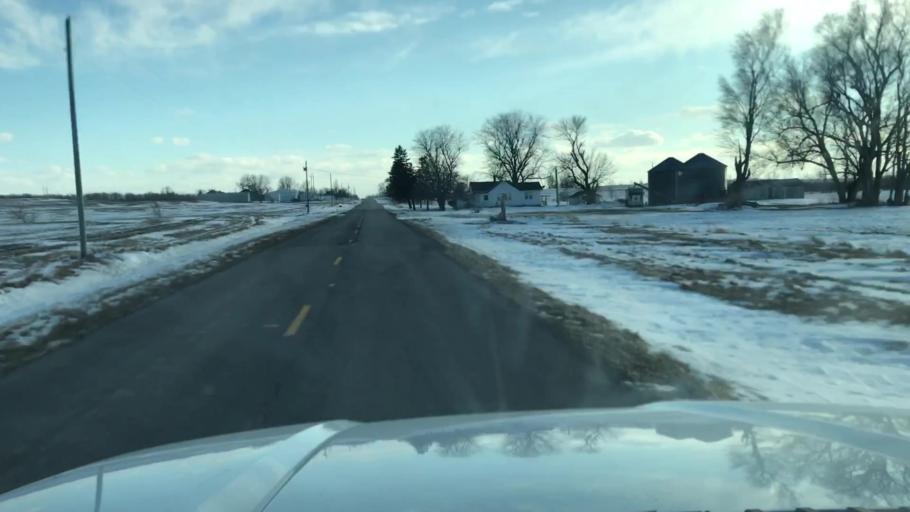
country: US
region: Missouri
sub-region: Holt County
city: Oregon
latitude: 40.1183
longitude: -95.0226
